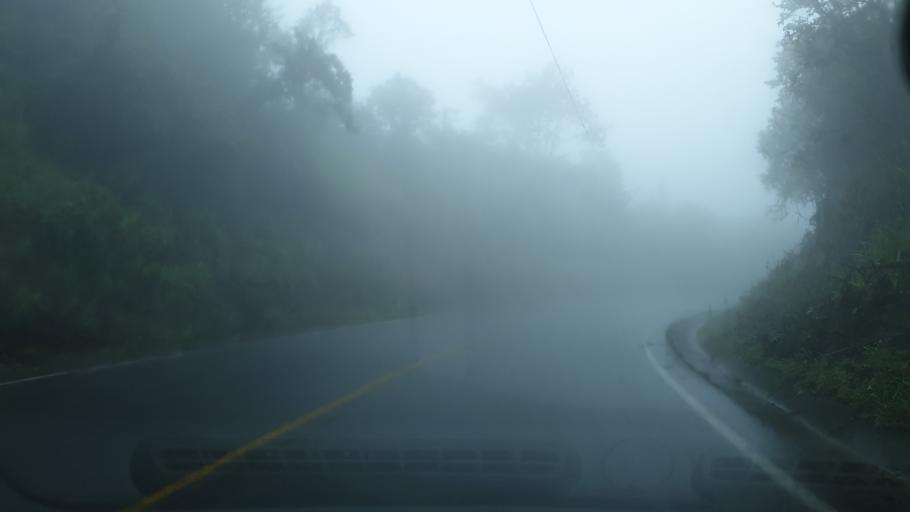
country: EC
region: Manabi
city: Jipijapa
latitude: -1.3467
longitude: -80.6548
